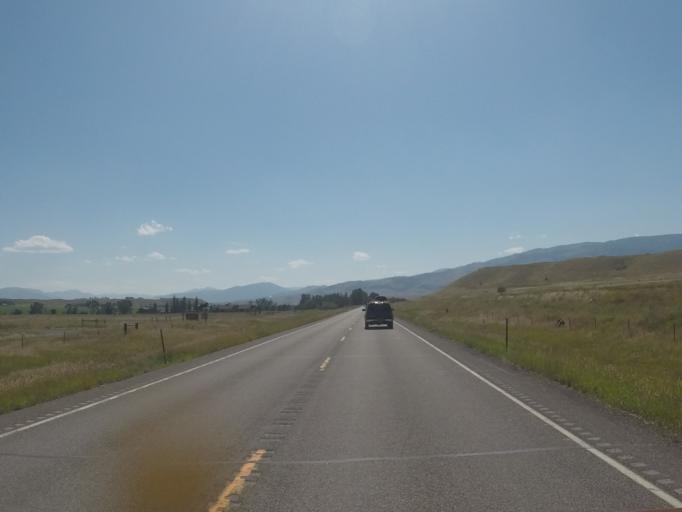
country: US
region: Montana
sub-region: Park County
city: Livingston
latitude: 45.4221
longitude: -110.6590
